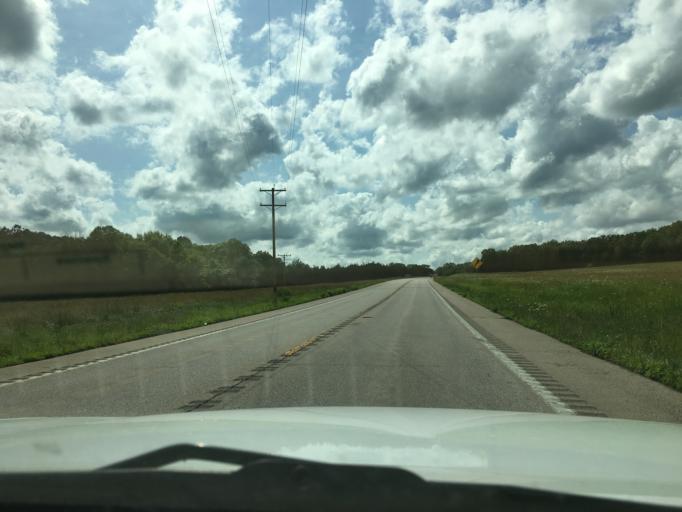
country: US
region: Missouri
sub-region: Franklin County
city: Gerald
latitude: 38.4201
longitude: -91.2536
